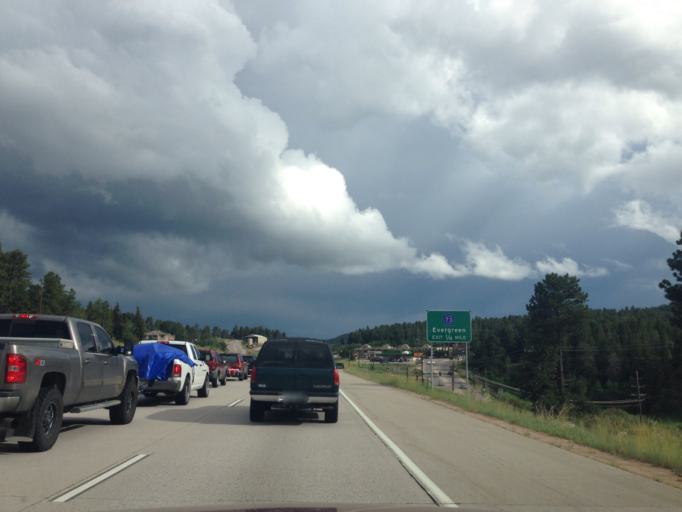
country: US
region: Colorado
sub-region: Jefferson County
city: Evergreen
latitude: 39.5238
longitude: -105.3067
